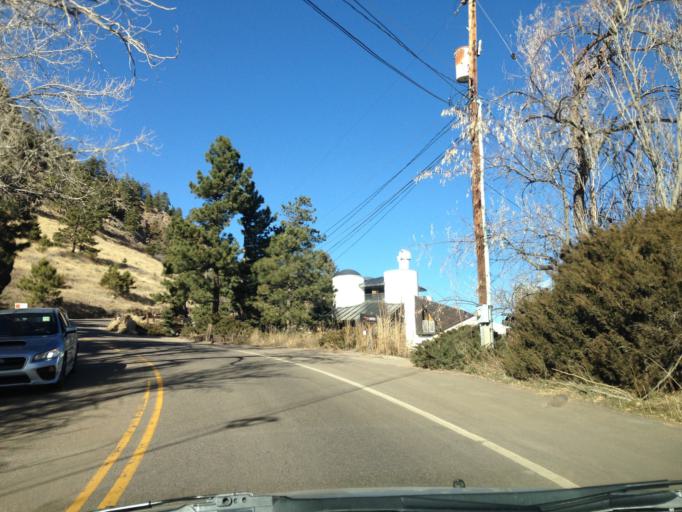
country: US
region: Colorado
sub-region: Boulder County
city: Boulder
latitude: 40.0009
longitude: -105.2904
